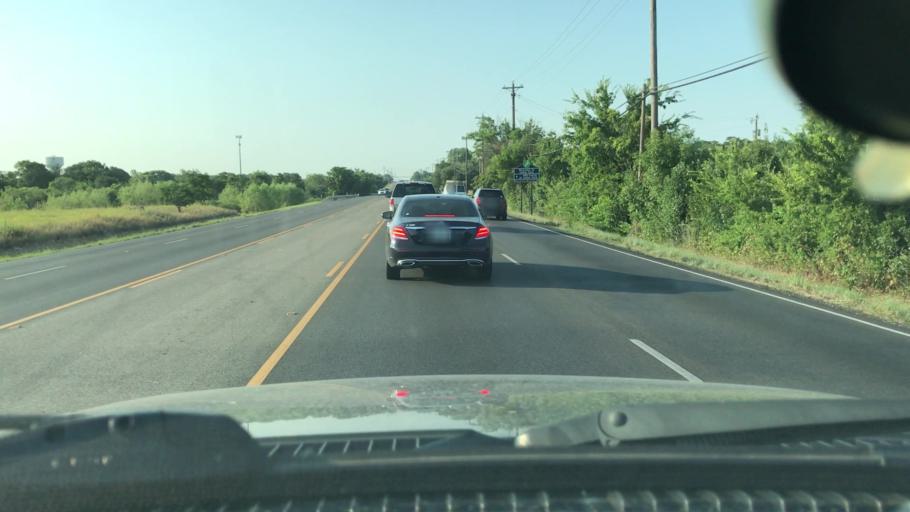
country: US
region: Texas
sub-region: Williamson County
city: Cedar Park
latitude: 30.5412
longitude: -97.8370
